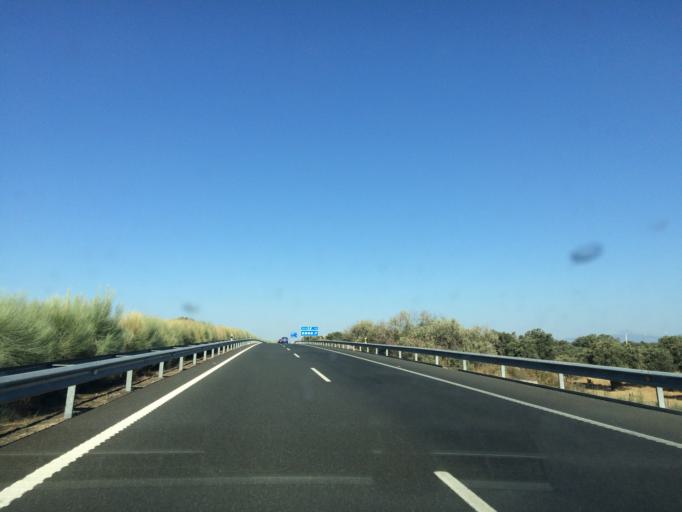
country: ES
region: Extremadura
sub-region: Provincia de Caceres
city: Navalmoral de la Mata
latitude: 39.8885
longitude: -5.4947
